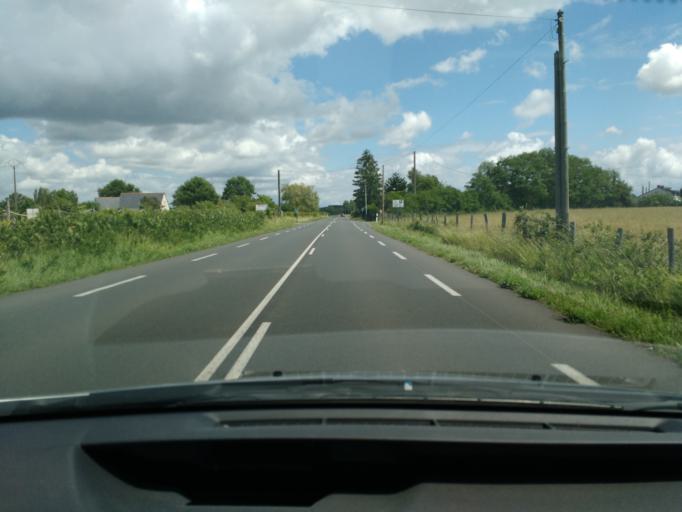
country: FR
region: Pays de la Loire
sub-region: Departement de Maine-et-Loire
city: Le Plessis-Grammoire
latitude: 47.4923
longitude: -0.4596
